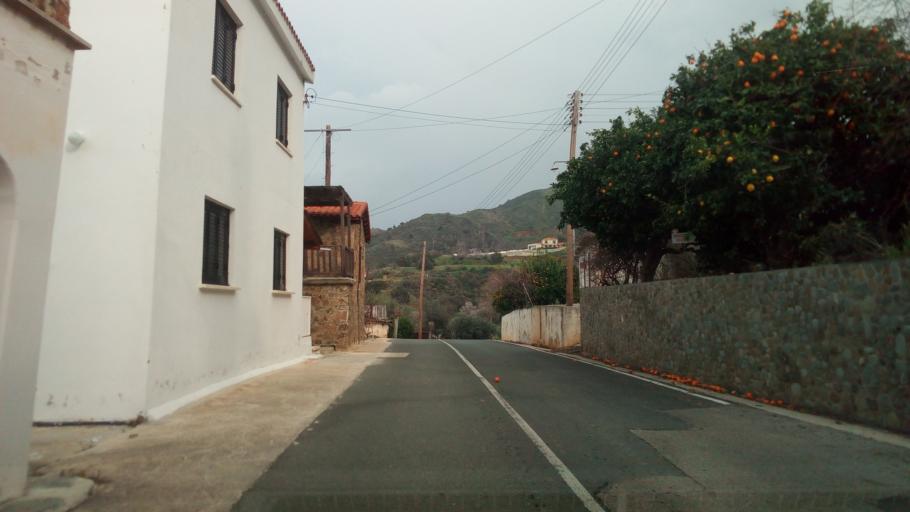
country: CY
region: Lefkosia
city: Kato Pyrgos
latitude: 35.1709
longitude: 32.5858
